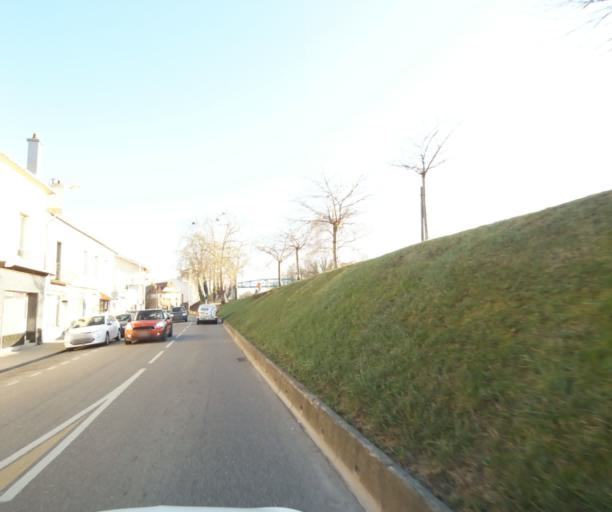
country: FR
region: Lorraine
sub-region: Departement de Meurthe-et-Moselle
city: Malzeville
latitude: 48.7002
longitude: 6.1890
